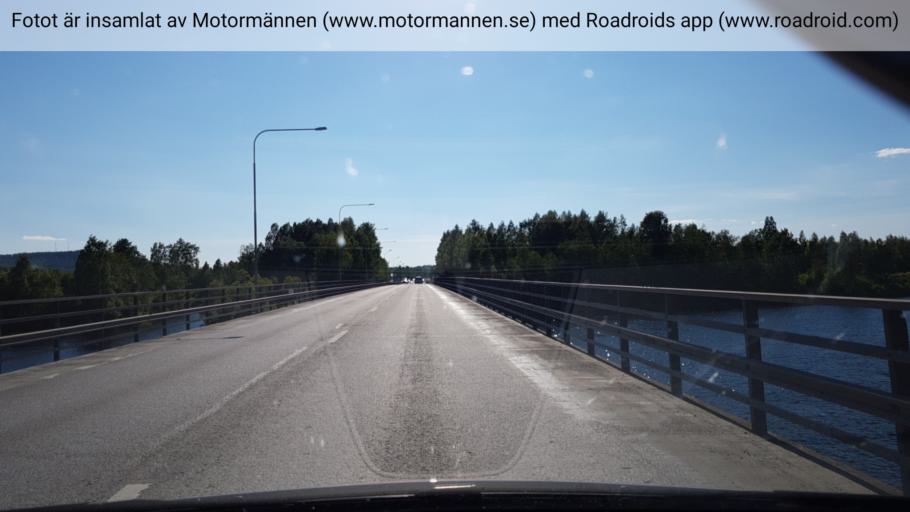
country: SE
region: Vaesterbotten
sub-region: Vannas Kommun
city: Vannasby
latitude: 63.9215
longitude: 19.8553
